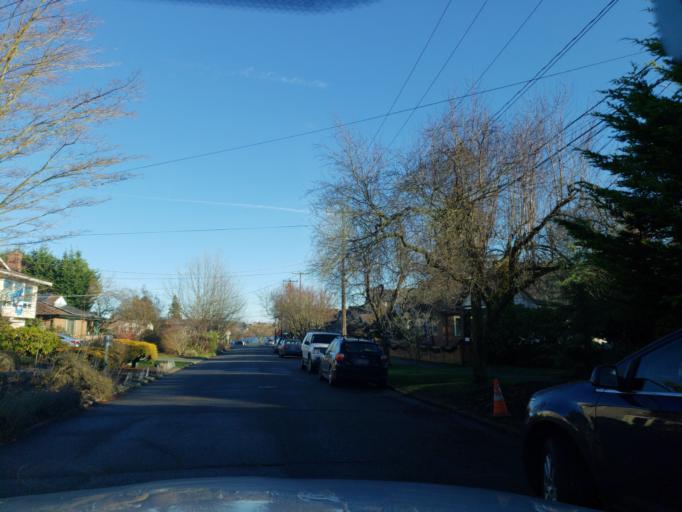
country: US
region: Washington
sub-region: King County
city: Seattle
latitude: 47.6778
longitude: -122.3488
